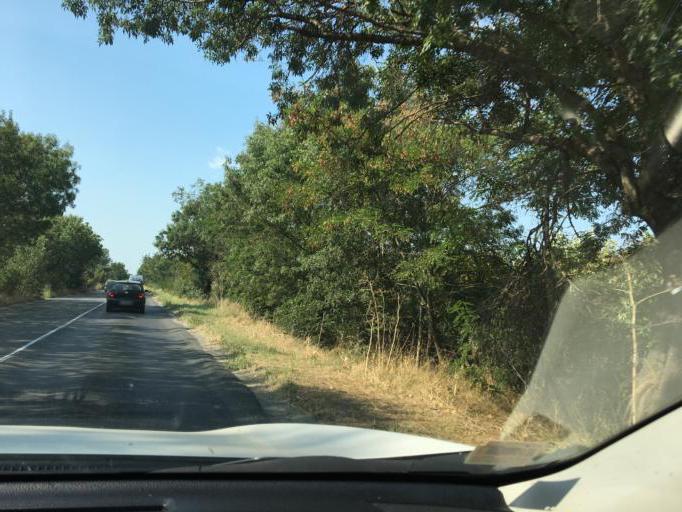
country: BG
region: Burgas
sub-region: Obshtina Burgas
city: Burgas
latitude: 42.5607
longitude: 27.4930
